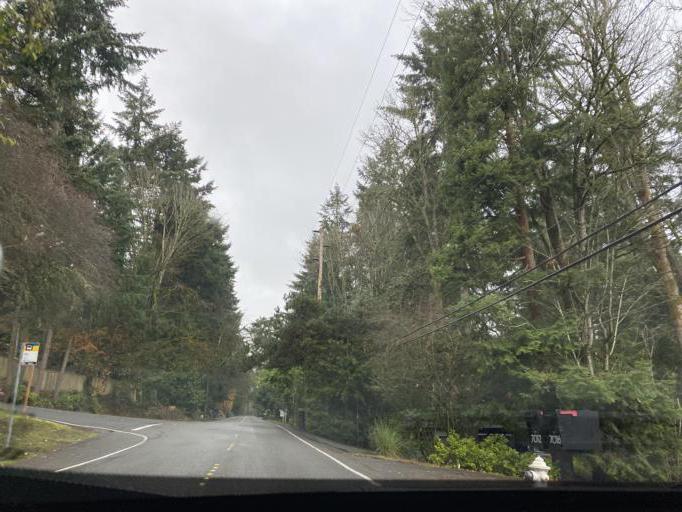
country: US
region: Washington
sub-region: King County
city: Mercer Island
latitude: 47.5401
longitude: -122.2128
